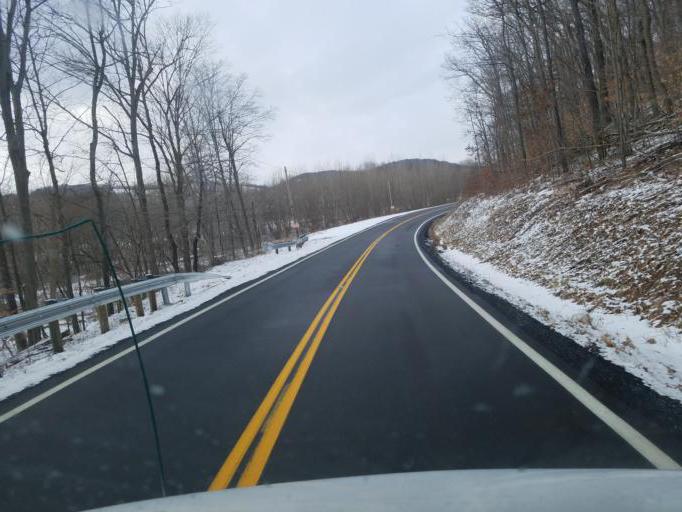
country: US
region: Ohio
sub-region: Holmes County
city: Millersburg
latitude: 40.4633
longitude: -81.9761
